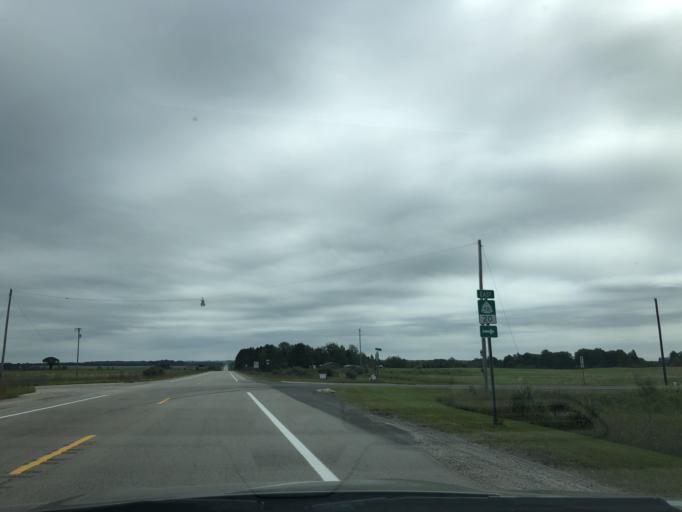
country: US
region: Michigan
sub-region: Clare County
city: Harrison
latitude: 44.0311
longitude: -84.9503
